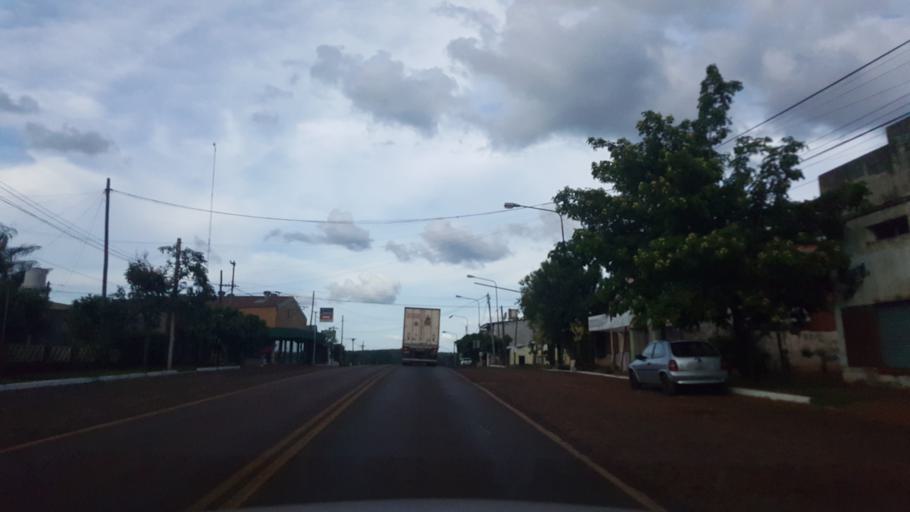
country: AR
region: Misiones
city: Gobernador Roca
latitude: -27.1859
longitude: -55.4640
